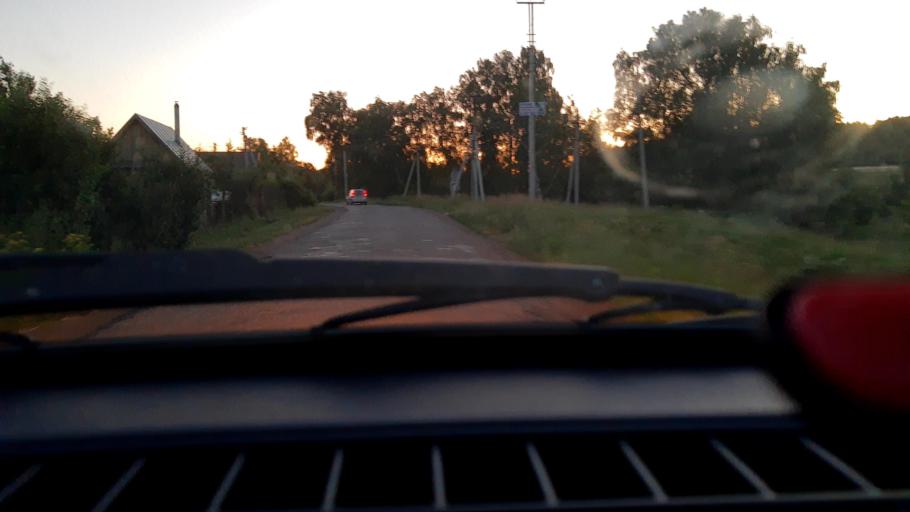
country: RU
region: Bashkortostan
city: Avdon
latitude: 54.4616
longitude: 55.8476
